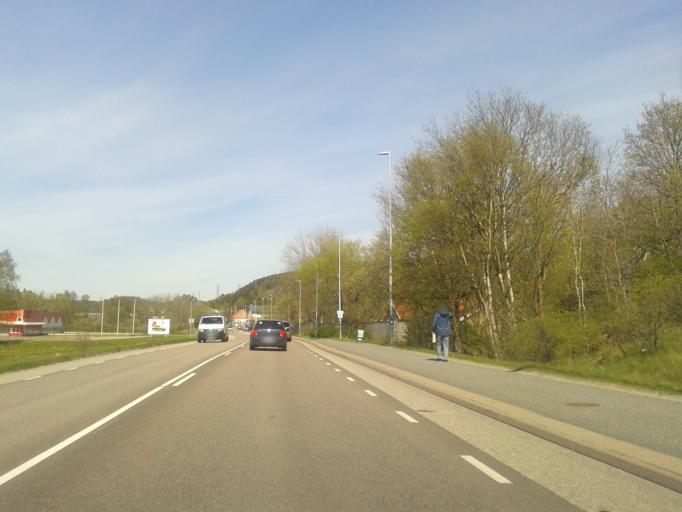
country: SE
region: Vaestra Goetaland
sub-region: Goteborg
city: Eriksbo
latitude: 57.7464
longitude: 12.0087
